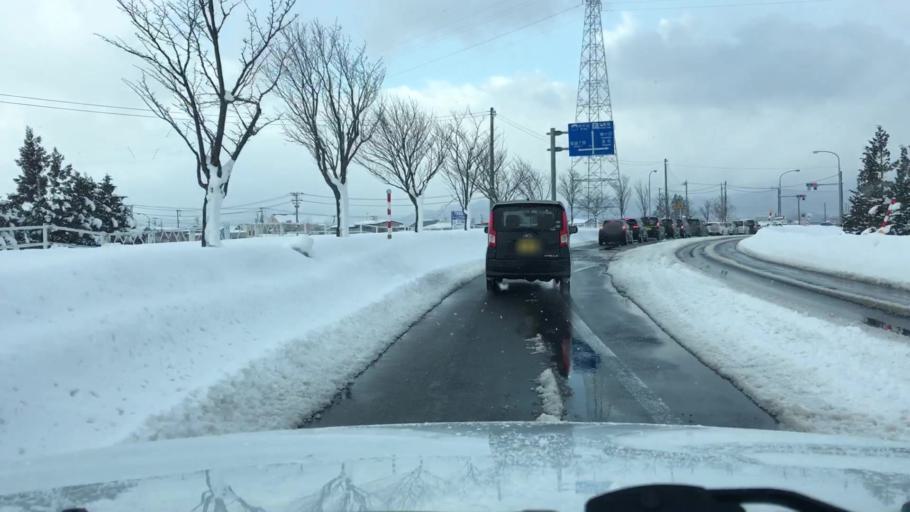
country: JP
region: Aomori
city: Hirosaki
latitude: 40.6291
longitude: 140.4743
